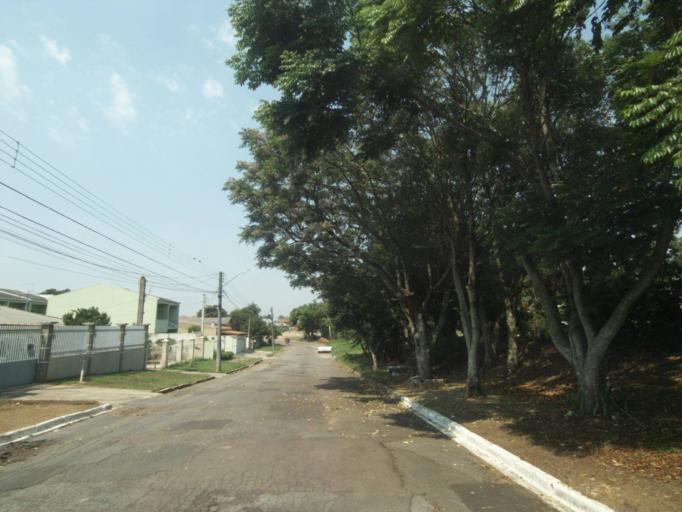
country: BR
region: Parana
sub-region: Sao Jose Dos Pinhais
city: Sao Jose dos Pinhais
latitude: -25.5443
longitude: -49.2471
